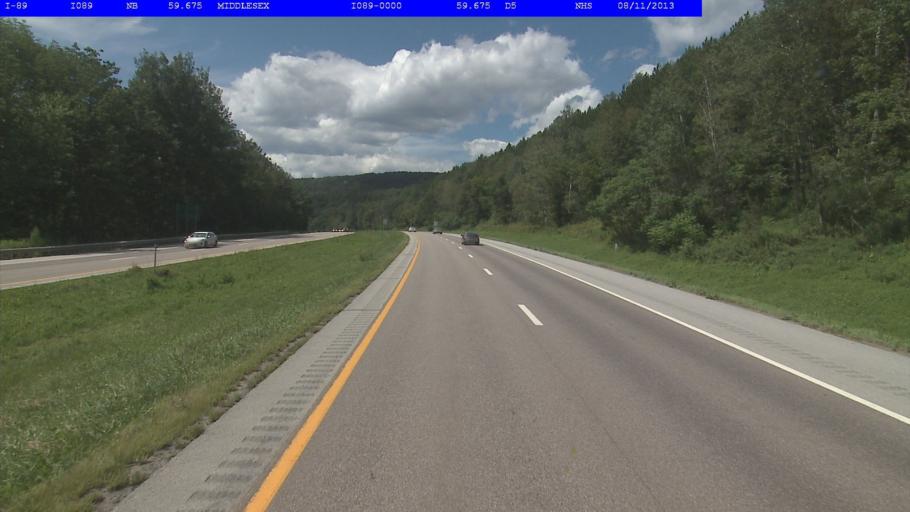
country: US
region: Vermont
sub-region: Washington County
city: Waterbury
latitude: 44.3106
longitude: -72.6936
